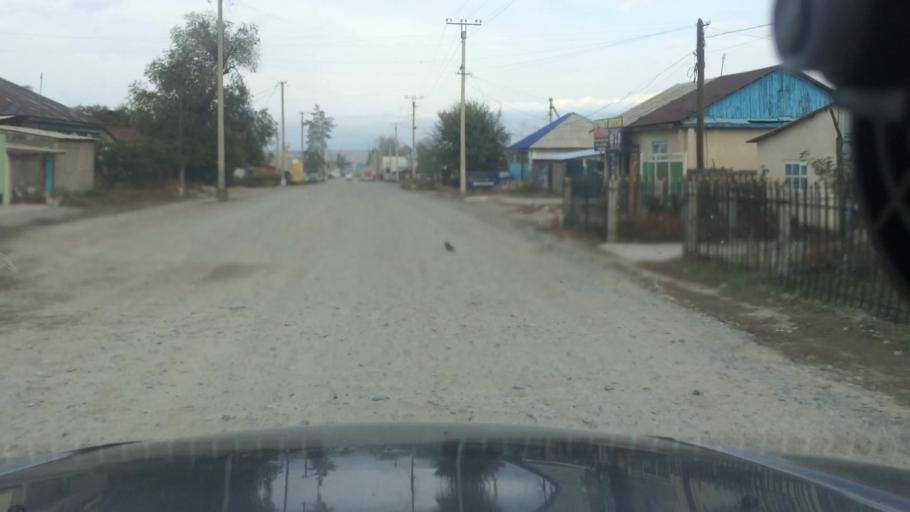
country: KG
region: Ysyk-Koel
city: Karakol
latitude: 42.4894
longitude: 78.3890
